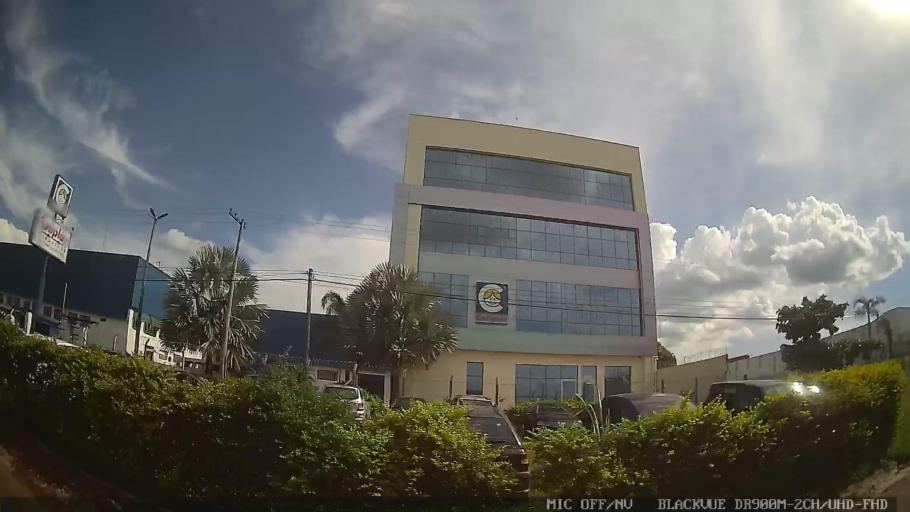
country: BR
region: Sao Paulo
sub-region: Laranjal Paulista
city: Laranjal Paulista
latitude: -23.0373
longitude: -47.8700
